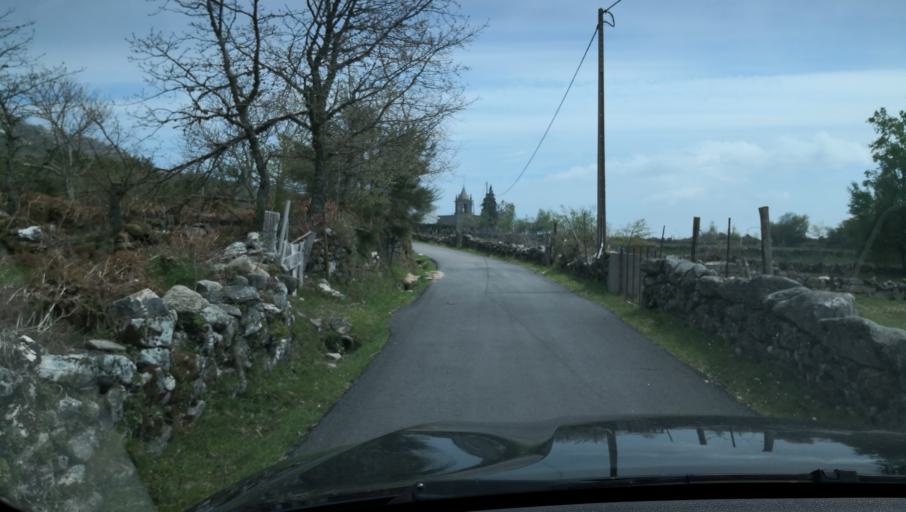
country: PT
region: Vila Real
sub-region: Vila Real
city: Vila Real
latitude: 41.2960
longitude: -7.8264
